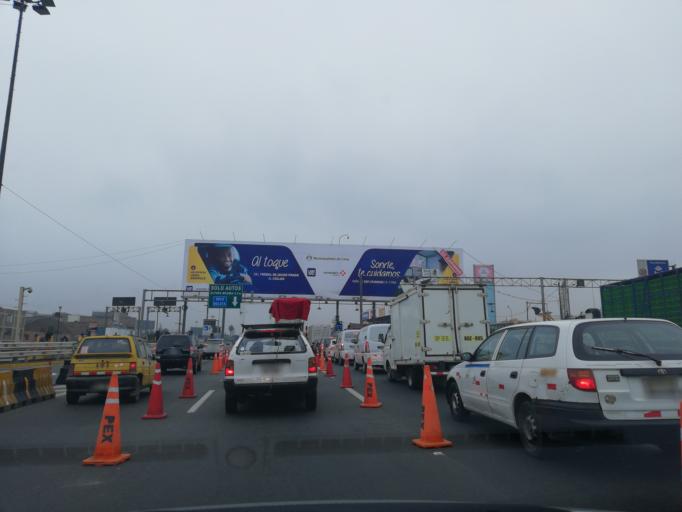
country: PE
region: Lima
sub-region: Lima
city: San Luis
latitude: -12.0676
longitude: -76.9716
